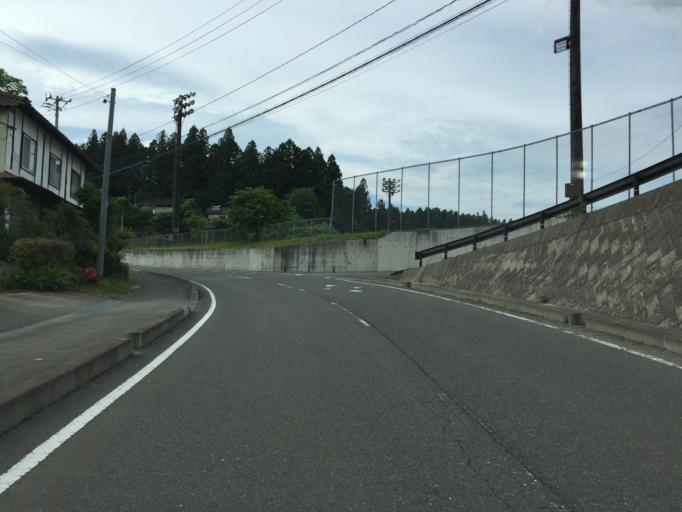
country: JP
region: Fukushima
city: Funehikimachi-funehiki
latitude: 37.5256
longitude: 140.5628
